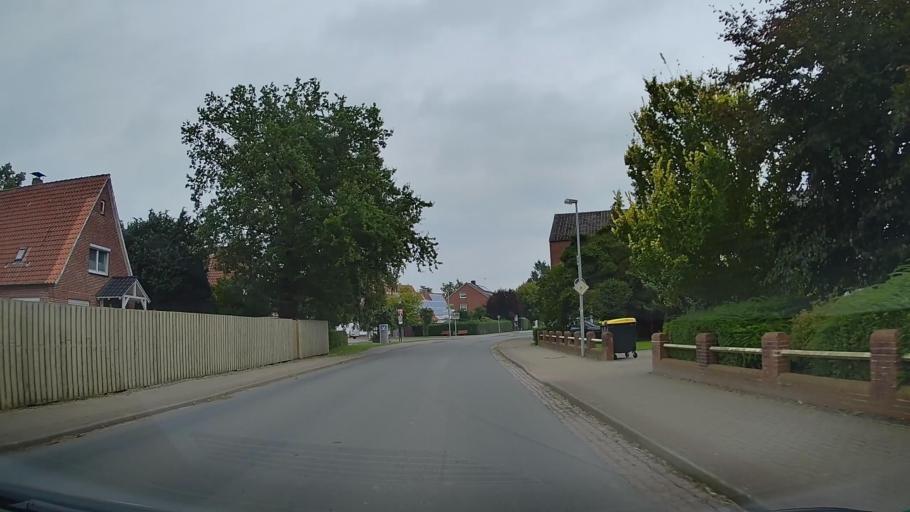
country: DE
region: Lower Saxony
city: Freiburg
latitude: 53.8243
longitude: 9.2830
